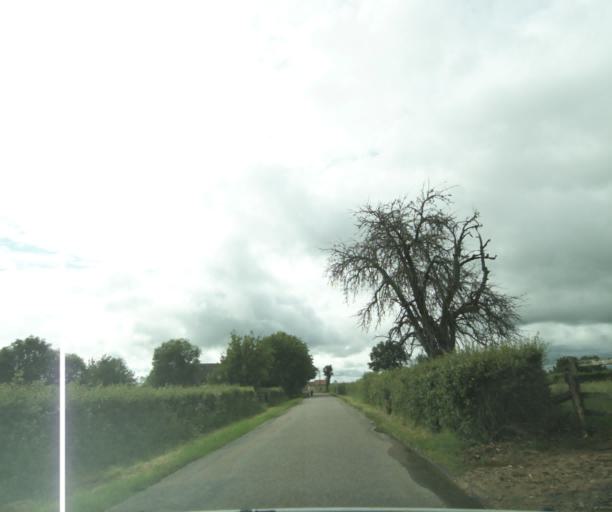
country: FR
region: Bourgogne
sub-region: Departement de Saone-et-Loire
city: Charolles
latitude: 46.4256
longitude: 4.2967
